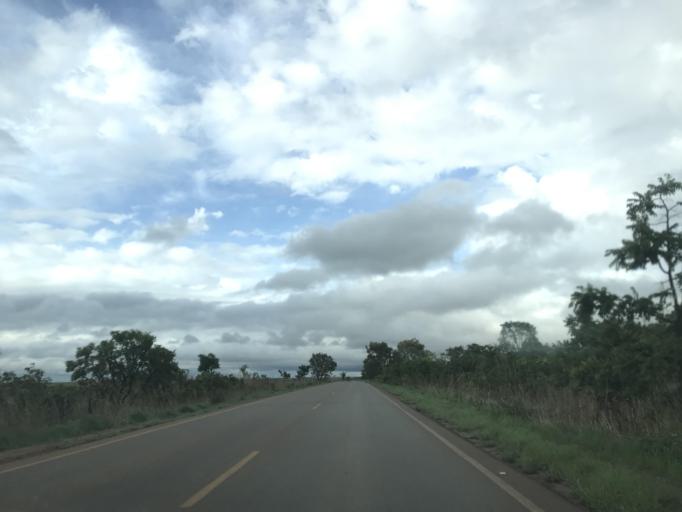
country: BR
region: Goias
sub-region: Vianopolis
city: Vianopolis
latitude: -16.5720
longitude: -48.2934
